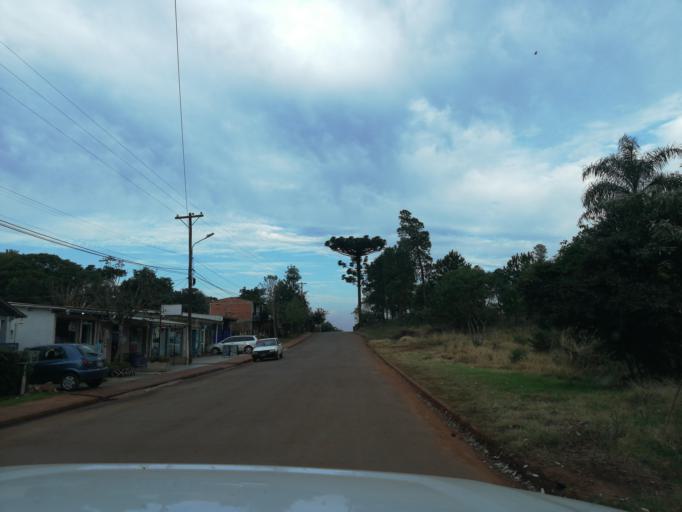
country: AR
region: Misiones
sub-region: Departamento de San Pedro
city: San Pedro
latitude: -26.6247
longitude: -54.0995
